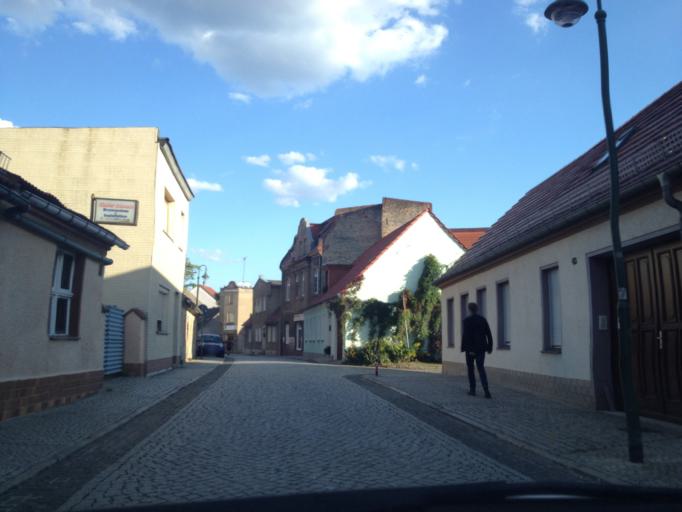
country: DE
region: Brandenburg
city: Vetschau
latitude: 51.7855
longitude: 14.0747
